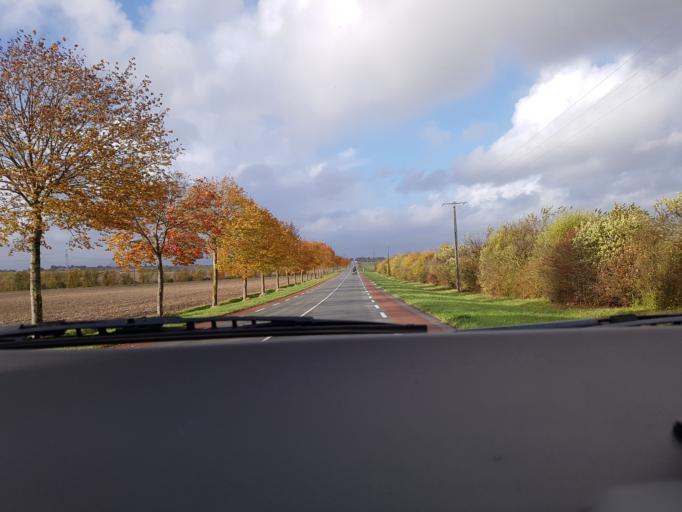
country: FR
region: Poitou-Charentes
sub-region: Departement de la Charente-Maritime
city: Les Gonds
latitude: 45.6564
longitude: -0.5897
